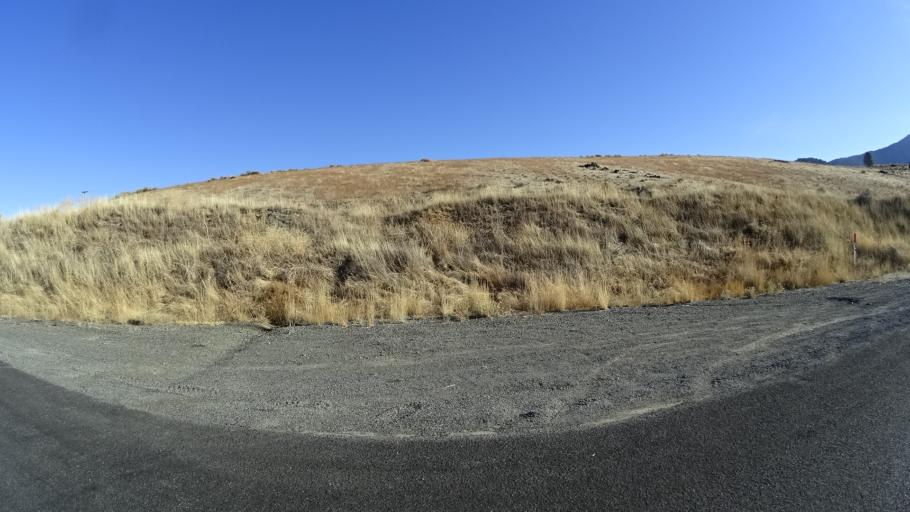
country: US
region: California
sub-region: Siskiyou County
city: Yreka
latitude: 41.4577
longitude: -122.8472
